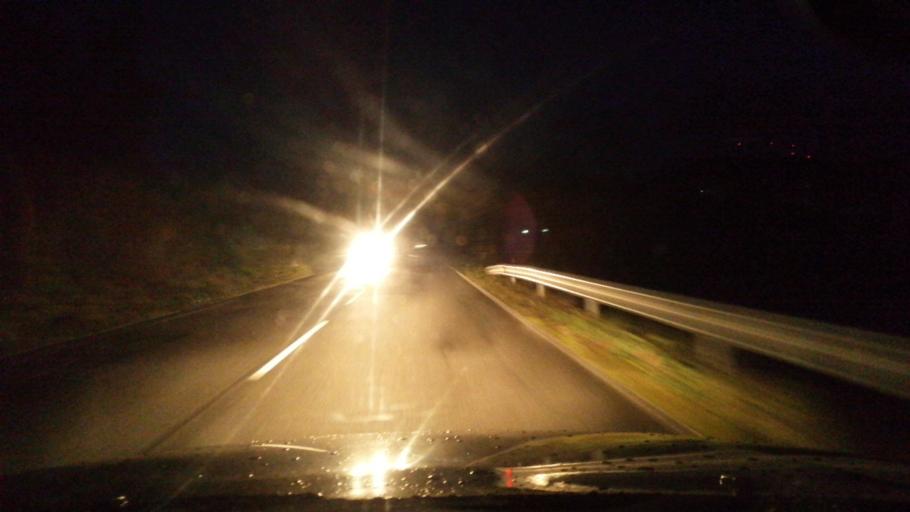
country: PT
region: Viseu
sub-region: Sao Joao da Pesqueira
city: Sao Joao da Pesqueira
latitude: 41.0941
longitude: -7.4747
